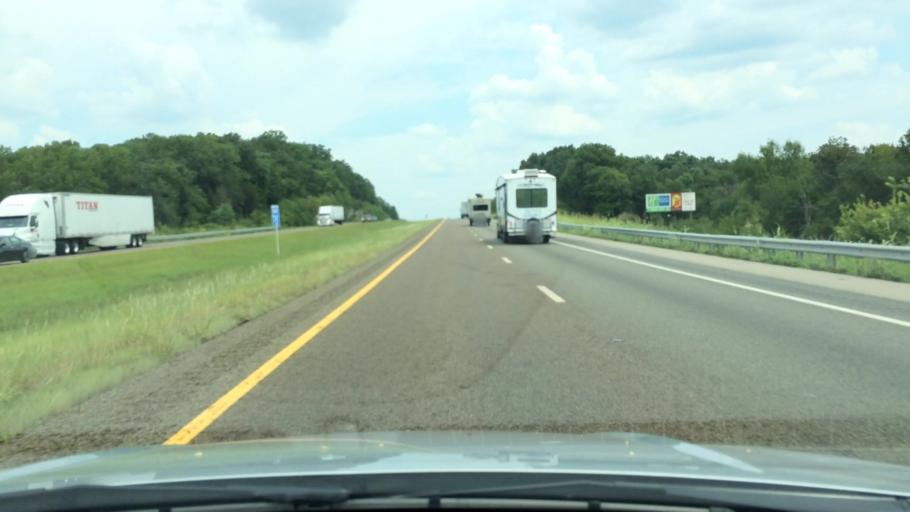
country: US
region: Tennessee
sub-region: Maury County
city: Columbia
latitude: 35.6064
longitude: -86.9010
